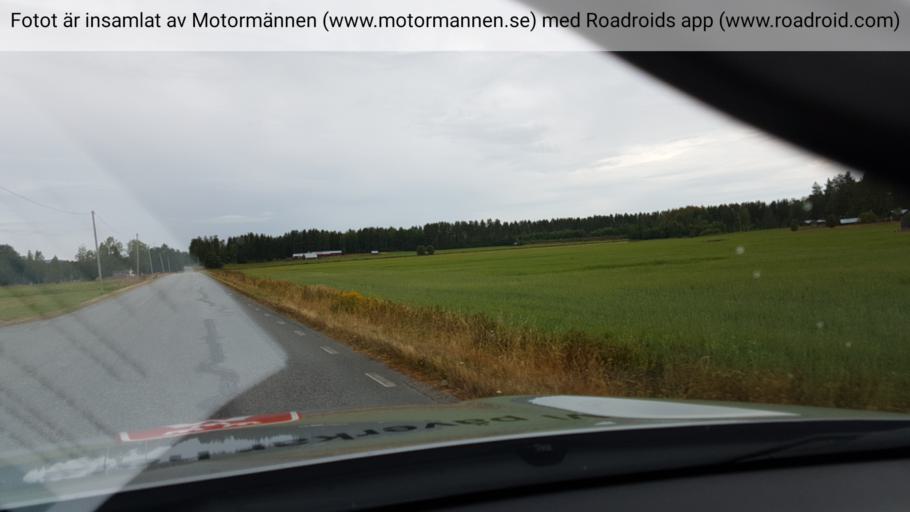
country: SE
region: Norrbotten
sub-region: Bodens Kommun
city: Boden
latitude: 65.8187
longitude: 21.5657
